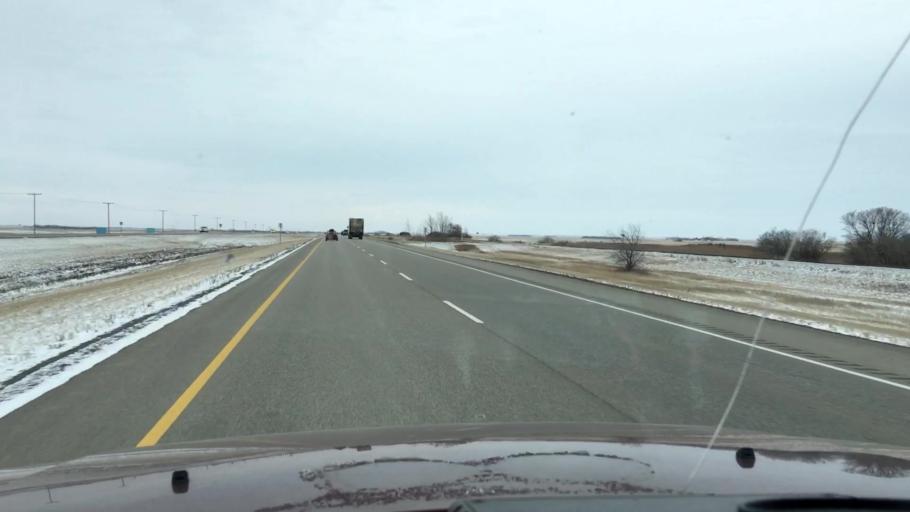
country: CA
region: Saskatchewan
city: Watrous
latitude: 51.1924
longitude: -105.9502
